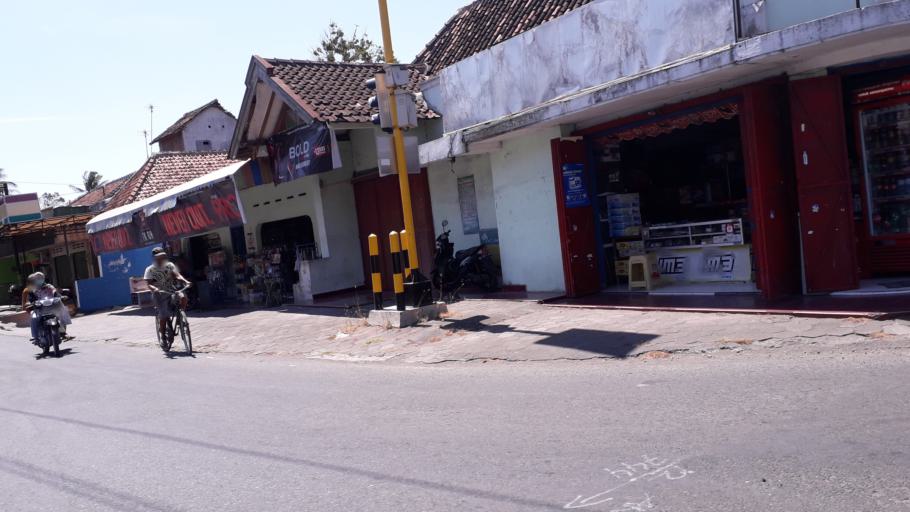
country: ID
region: Daerah Istimewa Yogyakarta
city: Pundong
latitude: -7.9787
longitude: 110.3173
